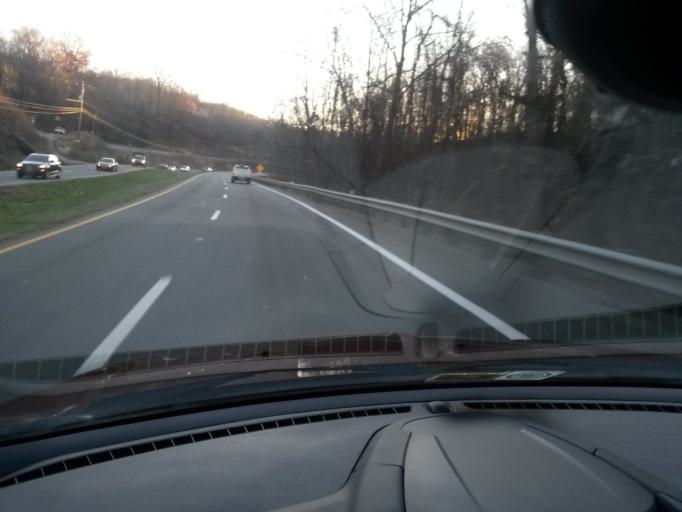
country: US
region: Virginia
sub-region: Roanoke County
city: Narrows
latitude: 37.1295
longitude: -79.9666
